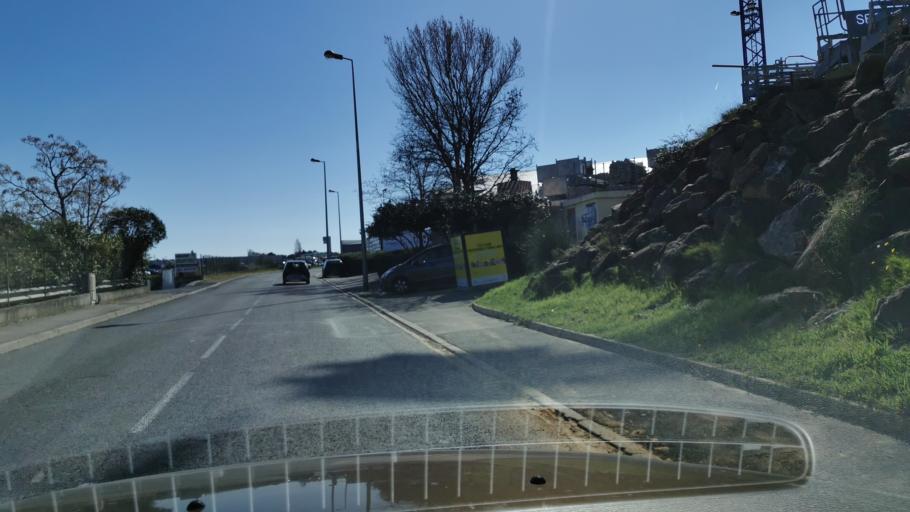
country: FR
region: Languedoc-Roussillon
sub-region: Departement de l'Aude
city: Narbonne
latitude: 43.1562
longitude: 2.9783
